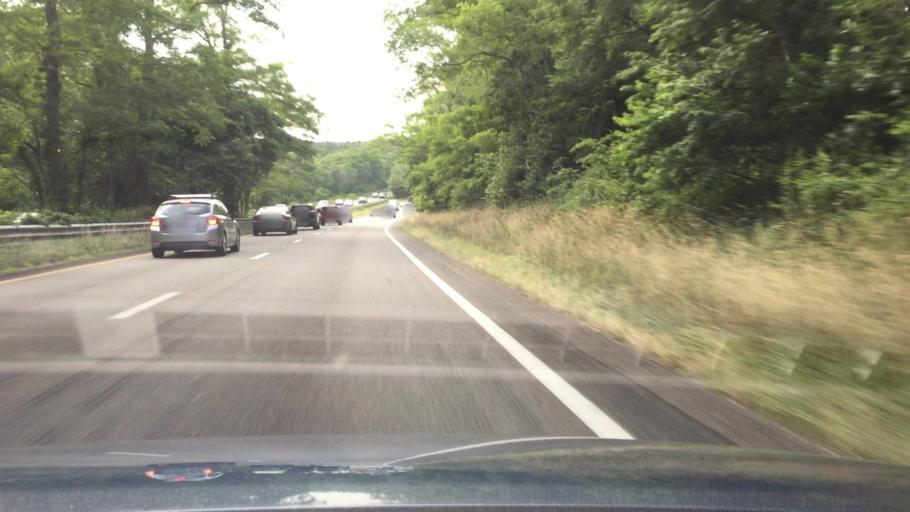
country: US
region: Massachusetts
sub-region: Barnstable County
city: Sandwich
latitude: 41.7438
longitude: -70.5095
